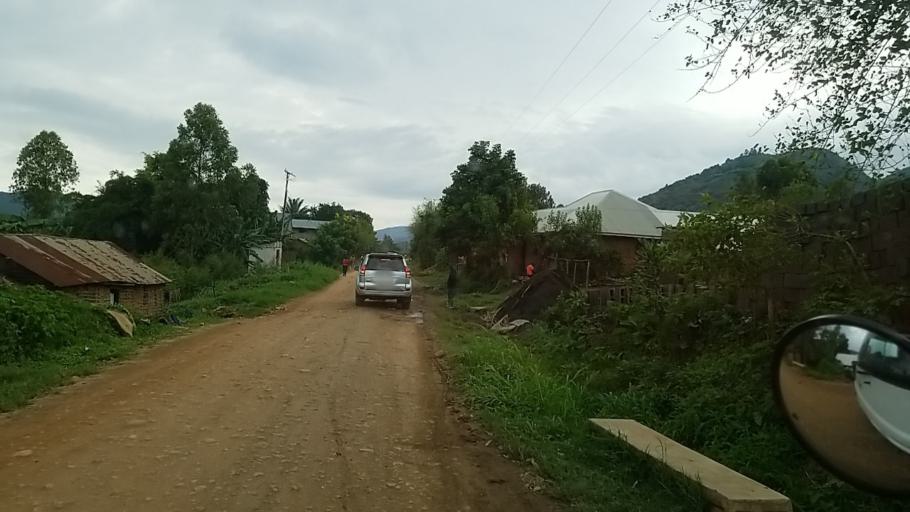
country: CD
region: Nord Kivu
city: Sake
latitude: -1.6763
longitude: 29.0169
